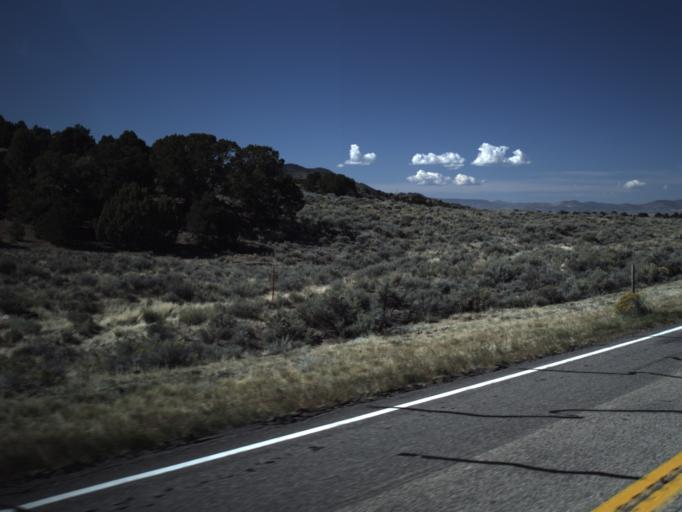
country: US
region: Utah
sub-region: Washington County
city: Enterprise
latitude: 37.6758
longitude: -113.4975
